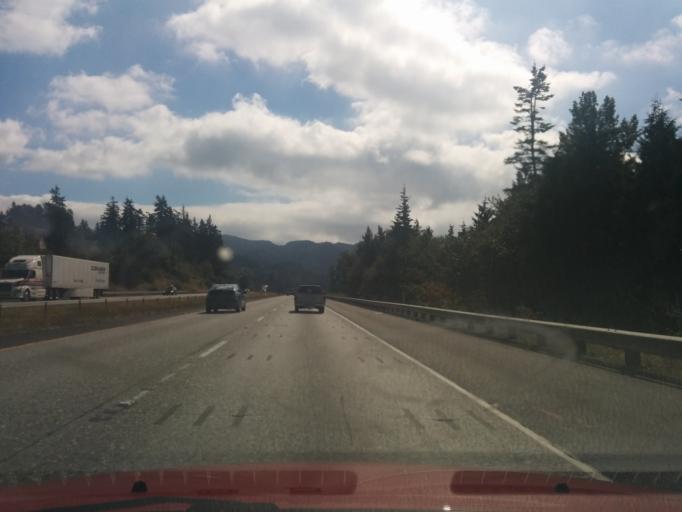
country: US
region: Washington
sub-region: Whatcom County
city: Bellingham
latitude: 48.7233
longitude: -122.4740
